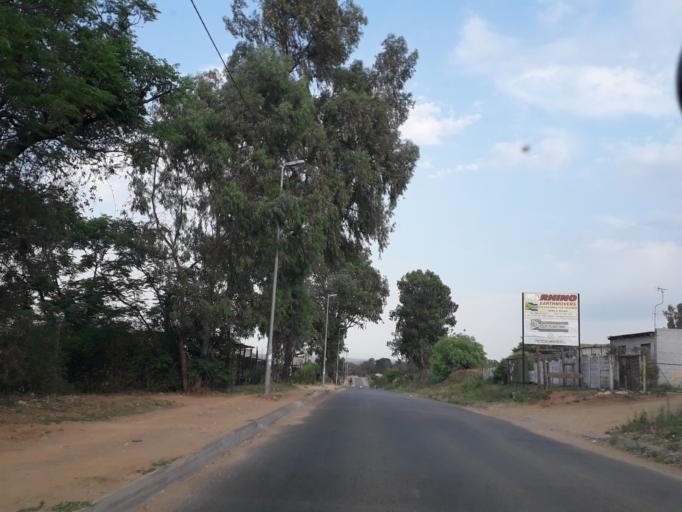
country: ZA
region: Gauteng
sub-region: West Rand District Municipality
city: Muldersdriseloop
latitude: -26.0761
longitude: 27.9083
